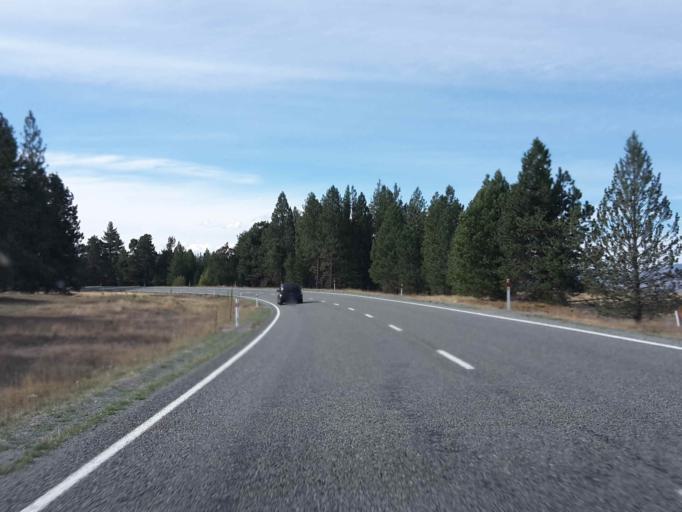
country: NZ
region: Canterbury
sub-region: Timaru District
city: Pleasant Point
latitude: -44.1809
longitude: 170.3172
